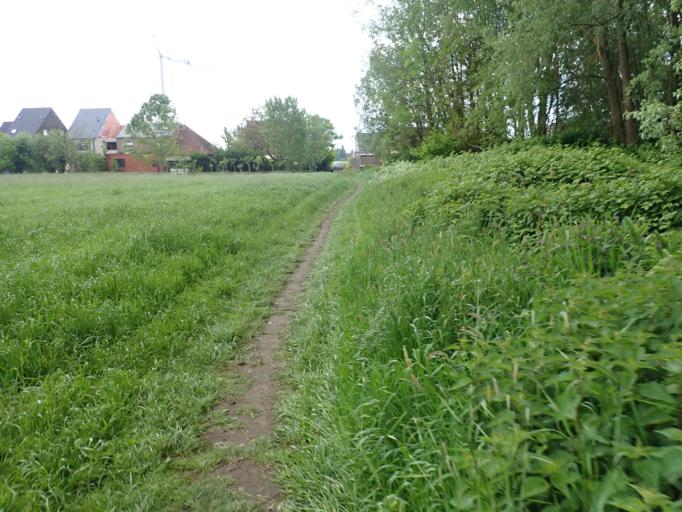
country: BE
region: Flanders
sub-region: Provincie Oost-Vlaanderen
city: Lebbeke
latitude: 51.0081
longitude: 4.1149
